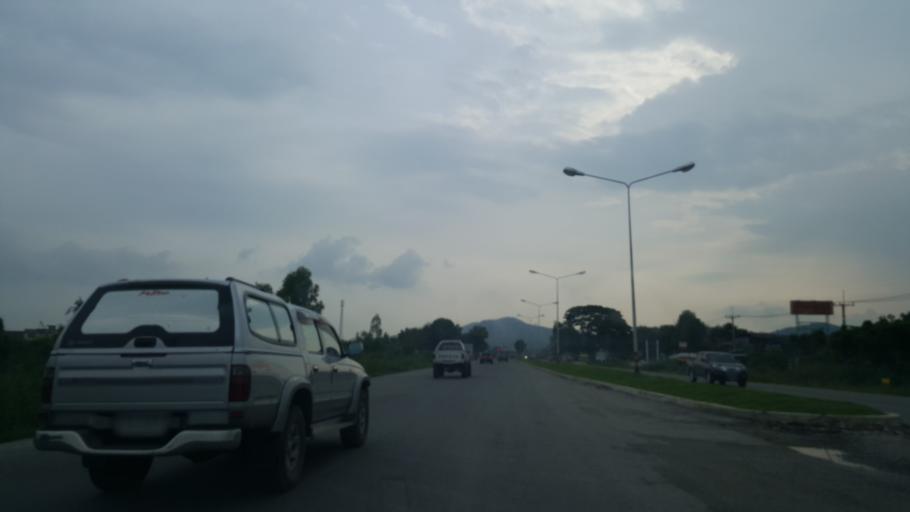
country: TH
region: Rayong
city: Ban Chang
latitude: 12.7287
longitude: 100.9838
